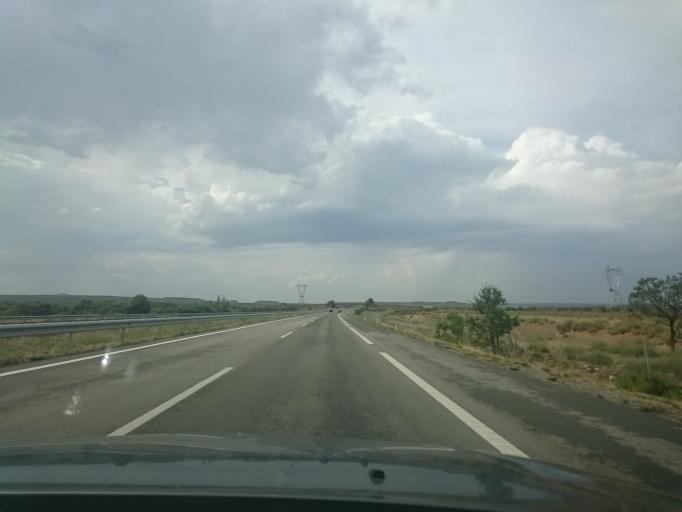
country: ES
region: La Rioja
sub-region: Provincia de La Rioja
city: Rincon de Soto
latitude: 42.1718
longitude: -1.8329
